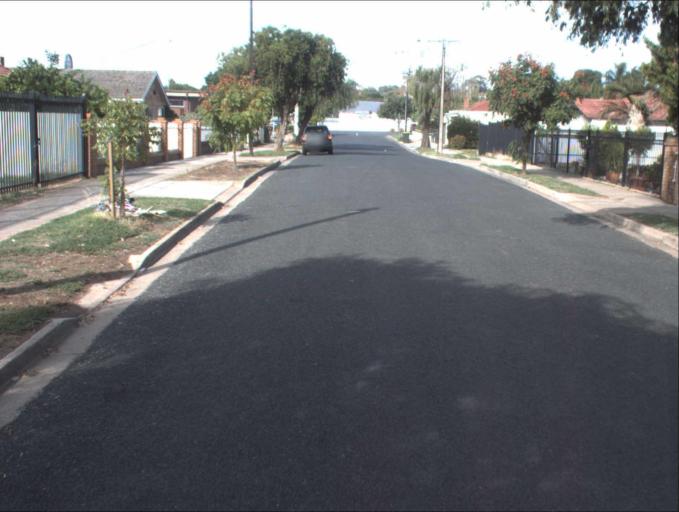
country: AU
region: South Australia
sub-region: Port Adelaide Enfield
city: Blair Athol
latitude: -34.8642
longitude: 138.5912
